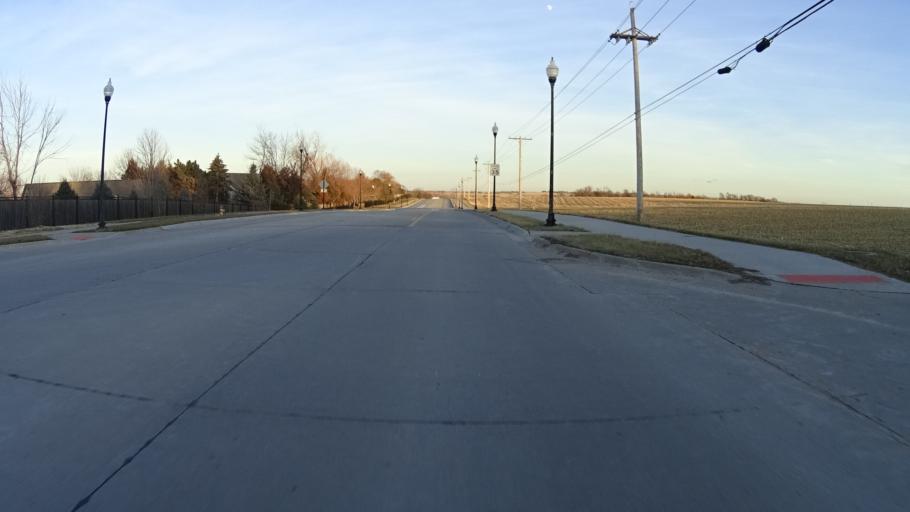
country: US
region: Nebraska
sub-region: Sarpy County
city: Papillion
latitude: 41.1326
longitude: -96.0526
